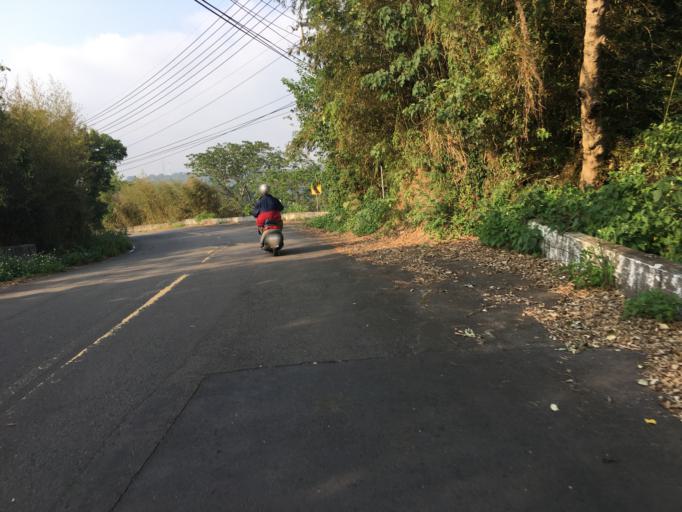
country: TW
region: Taiwan
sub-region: Hsinchu
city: Hsinchu
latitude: 24.7397
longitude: 121.0300
